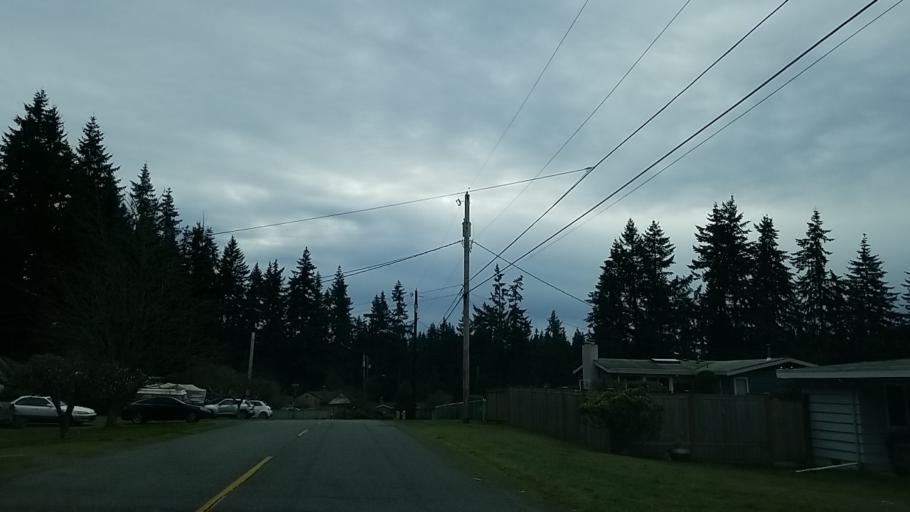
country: US
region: Washington
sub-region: Snohomish County
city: Esperance
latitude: 47.7844
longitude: -122.3620
